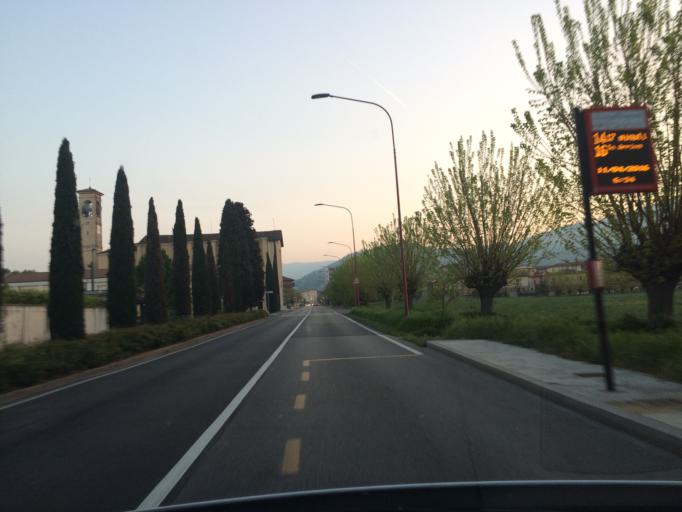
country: IT
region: Lombardy
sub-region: Provincia di Brescia
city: Brescia
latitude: 45.5168
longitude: 10.2280
